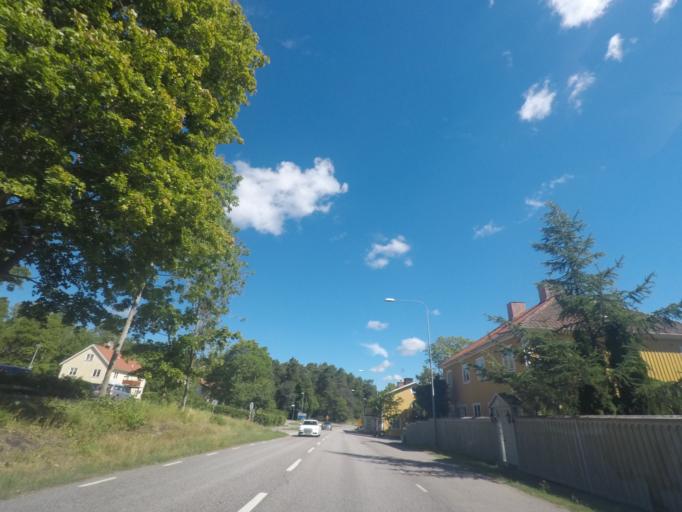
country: SE
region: Uppsala
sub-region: Knivsta Kommun
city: Knivsta
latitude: 59.8741
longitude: 17.9605
